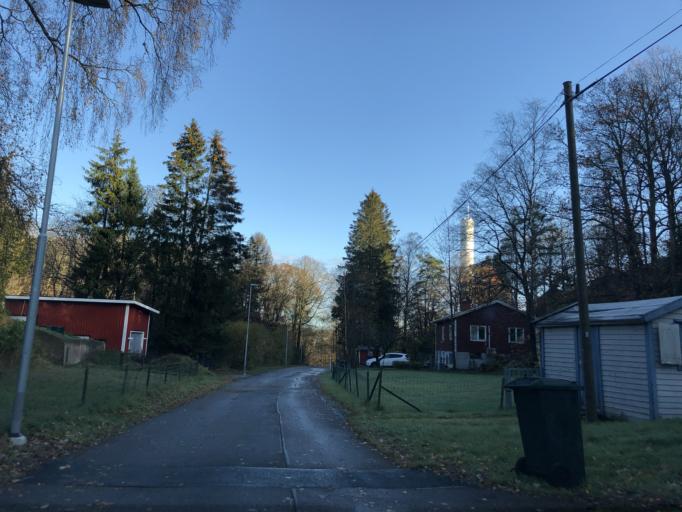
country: SE
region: Vaestra Goetaland
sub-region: Goteborg
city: Gardsten
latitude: 57.7992
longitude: 12.0385
